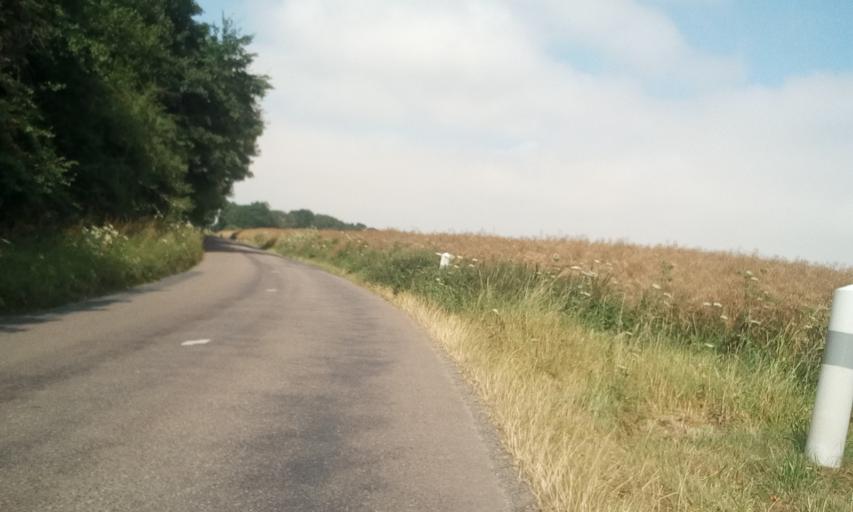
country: FR
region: Lower Normandy
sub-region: Departement du Calvados
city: Douvres-la-Delivrande
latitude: 49.2913
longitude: -0.4117
